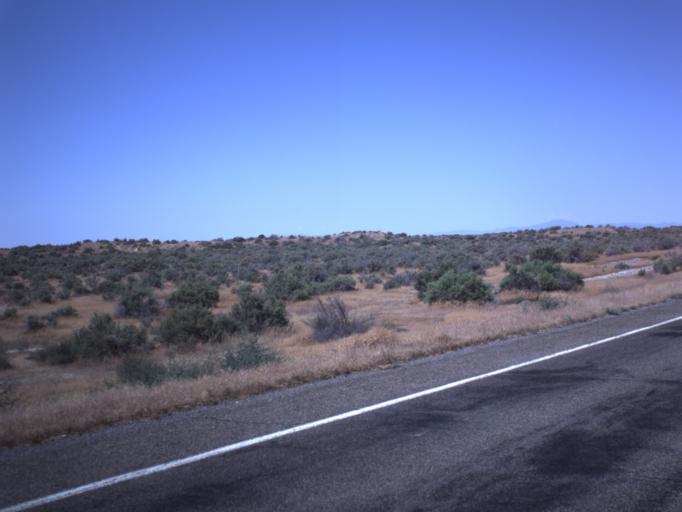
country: US
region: Utah
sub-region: Millard County
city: Delta
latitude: 39.4823
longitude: -112.5186
